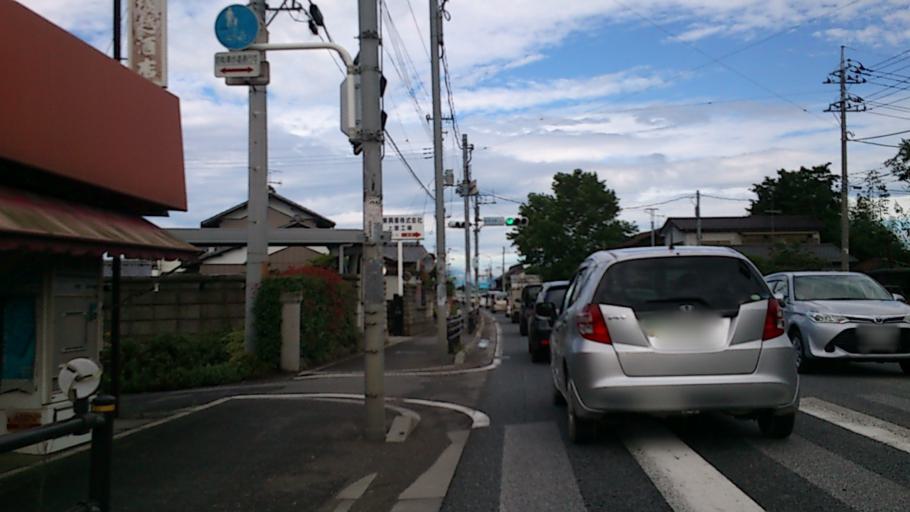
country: JP
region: Gunma
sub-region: Sawa-gun
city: Tamamura
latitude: 36.2657
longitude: 139.1268
